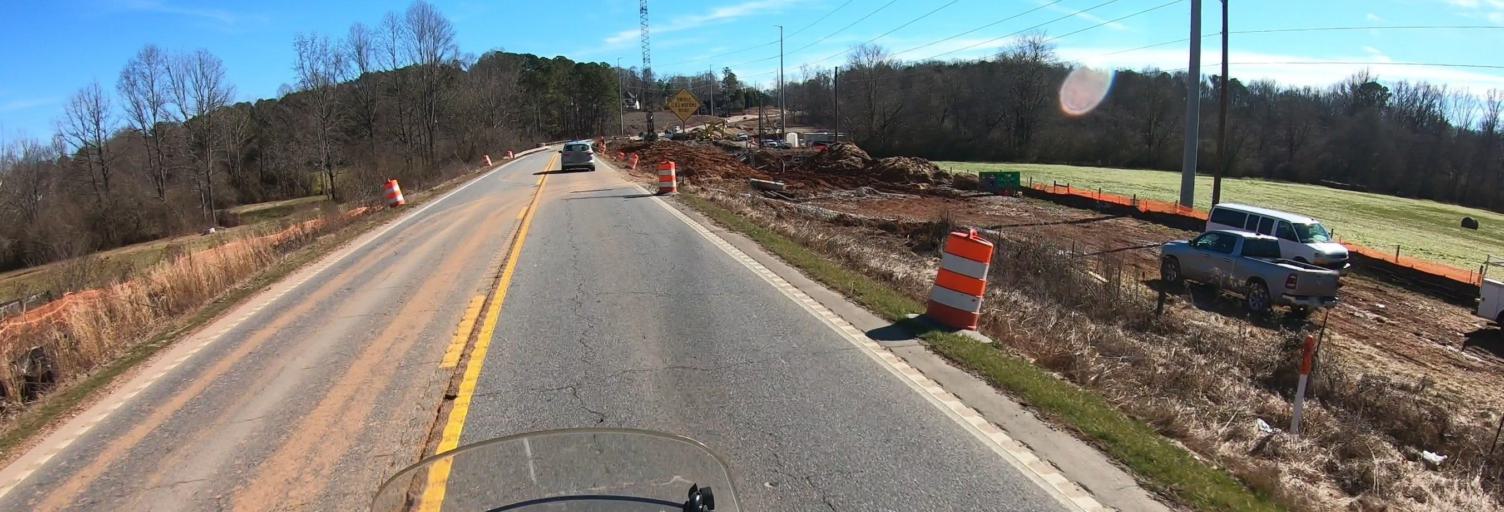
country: US
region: Georgia
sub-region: Forsyth County
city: Cumming
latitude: 34.2896
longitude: -84.1447
